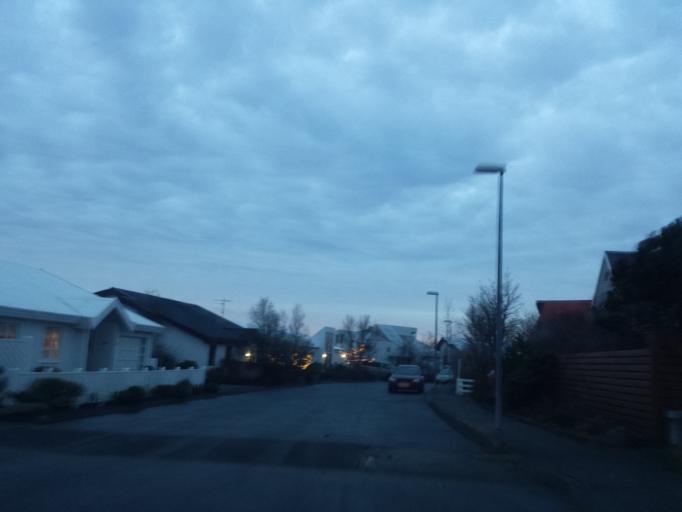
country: IS
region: Capital Region
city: Mosfellsbaer
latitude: 64.1362
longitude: -21.7747
